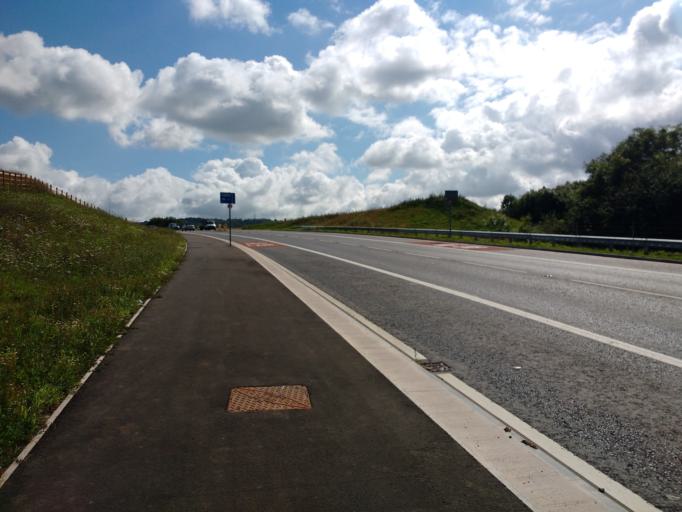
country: GB
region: England
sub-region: North Somerset
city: Dundry
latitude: 51.4218
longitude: -2.6376
